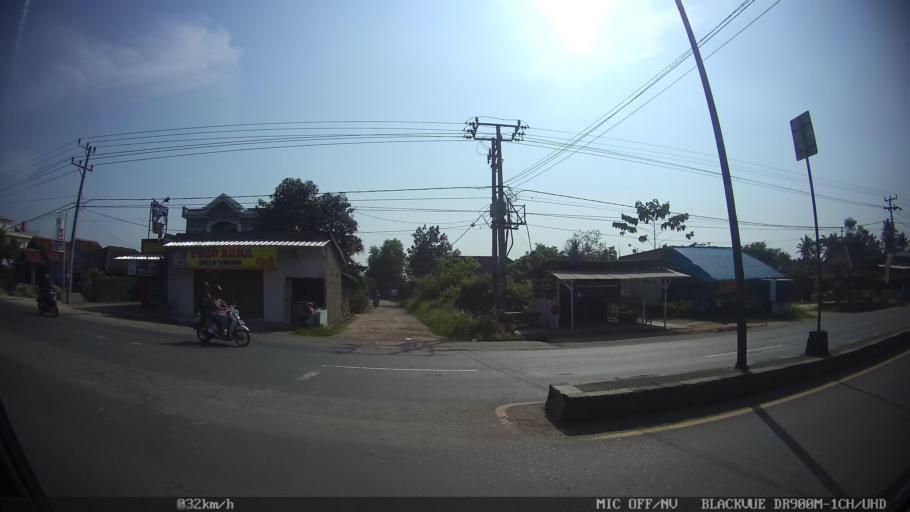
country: ID
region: Lampung
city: Natar
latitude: -5.2516
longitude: 105.1821
